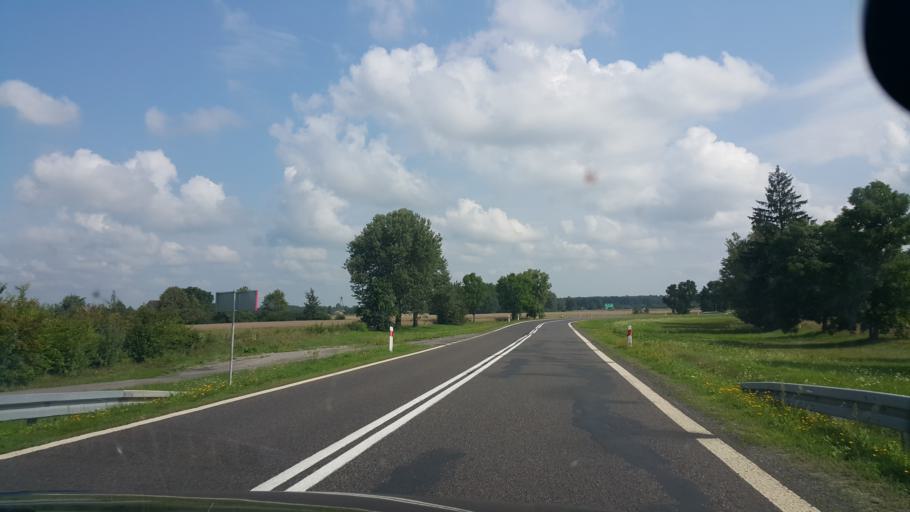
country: PL
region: Lublin Voivodeship
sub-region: Powiat wlodawski
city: Hansk
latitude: 51.4626
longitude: 23.3115
